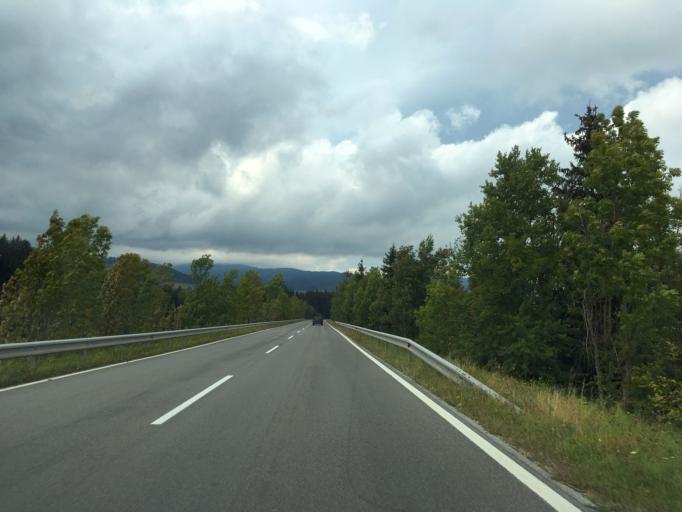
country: AT
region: Lower Austria
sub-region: Politischer Bezirk Neunkirchen
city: Monichkirchen
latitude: 47.4714
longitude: 16.0556
